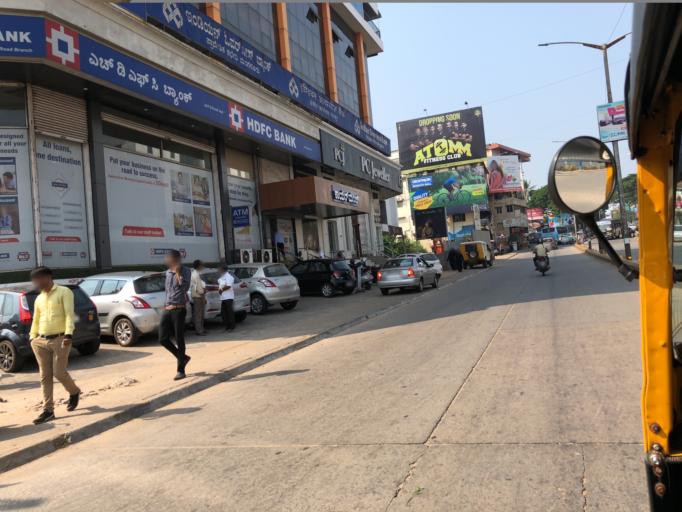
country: IN
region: Karnataka
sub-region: Dakshina Kannada
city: Mangalore
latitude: 12.8813
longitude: 74.8397
